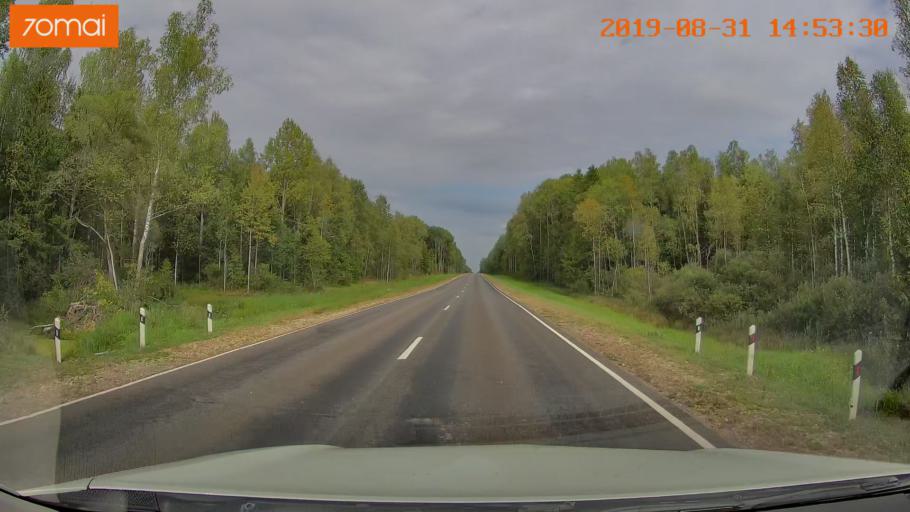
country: RU
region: Kaluga
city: Spas-Demensk
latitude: 54.2837
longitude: 33.8657
